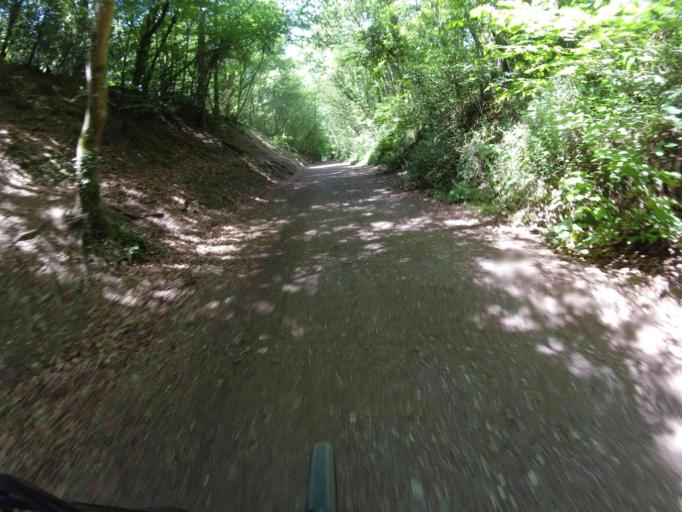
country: GB
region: England
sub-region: Devon
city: Bovey Tracey
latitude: 50.5979
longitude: -3.6869
